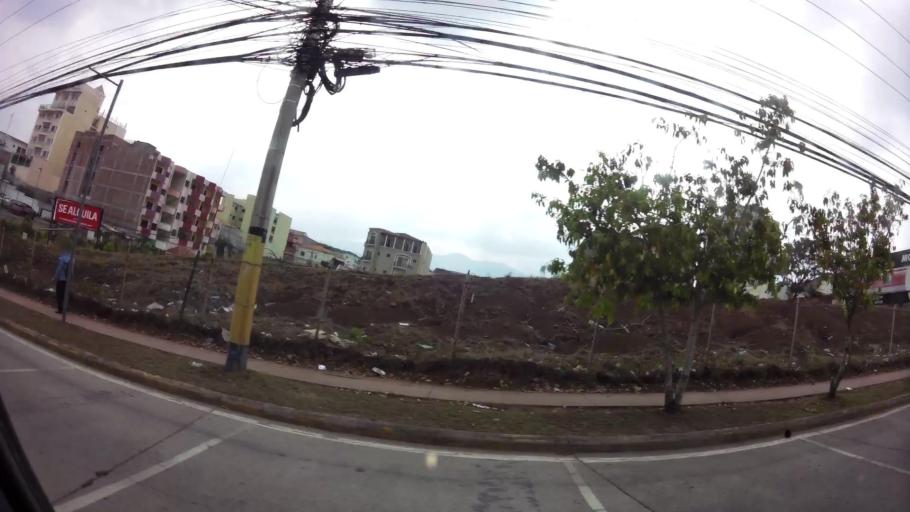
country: HN
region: Francisco Morazan
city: Tegucigalpa
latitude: 14.0864
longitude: -87.1739
